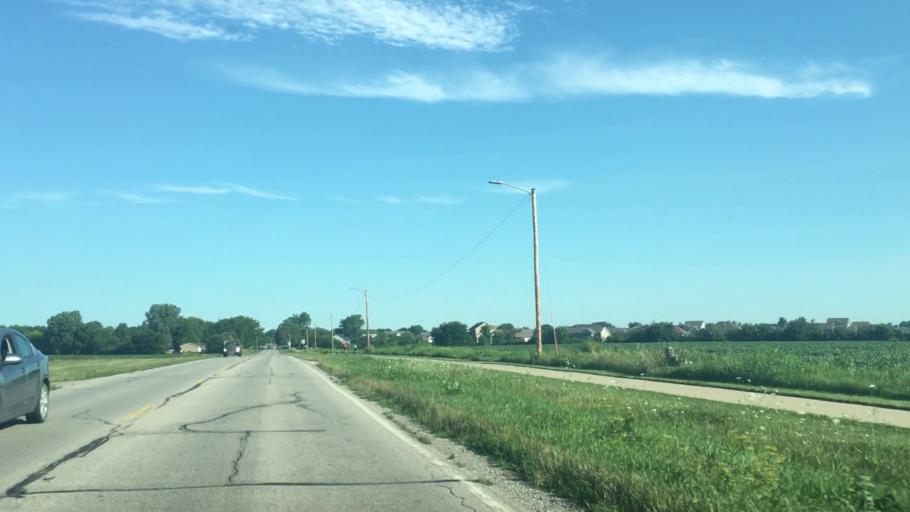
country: US
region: Iowa
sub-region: Johnson County
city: North Liberty
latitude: 41.7385
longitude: -91.5853
